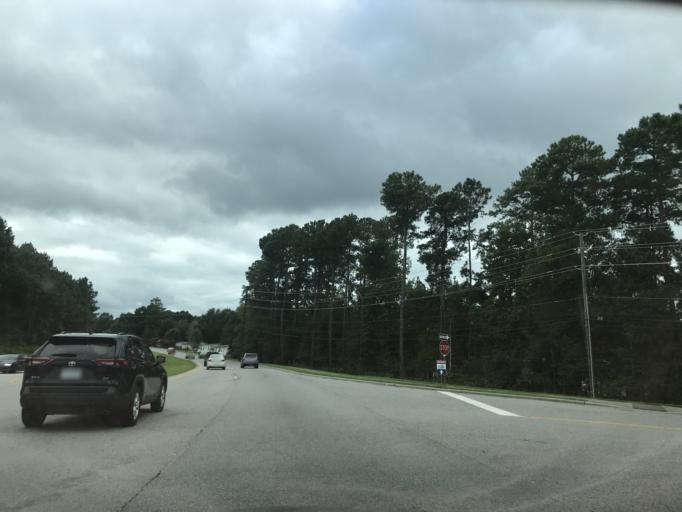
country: US
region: North Carolina
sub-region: Wake County
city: Garner
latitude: 35.7377
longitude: -78.5718
